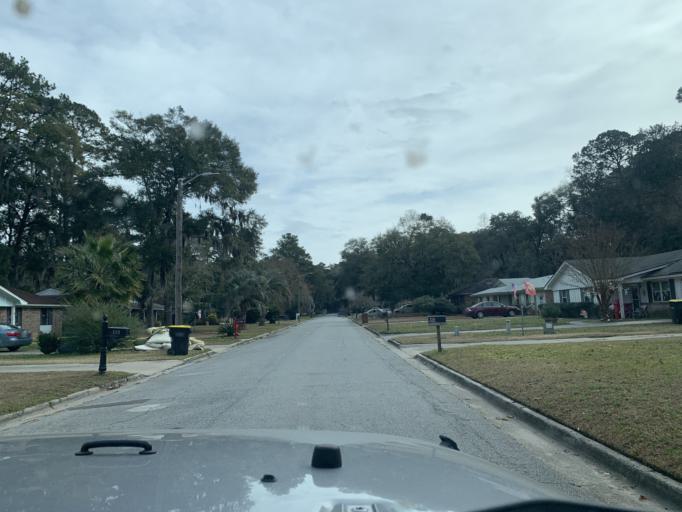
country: US
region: Georgia
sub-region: Chatham County
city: Montgomery
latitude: 31.9671
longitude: -81.1287
